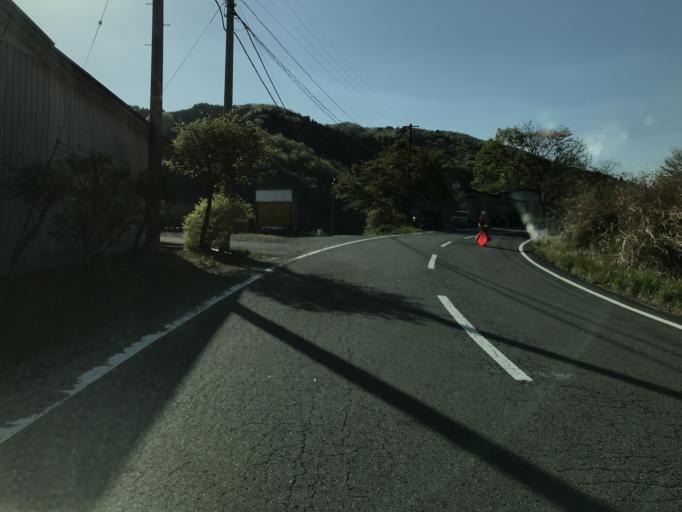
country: JP
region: Fukushima
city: Funehikimachi-funehiki
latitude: 37.5066
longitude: 140.7616
